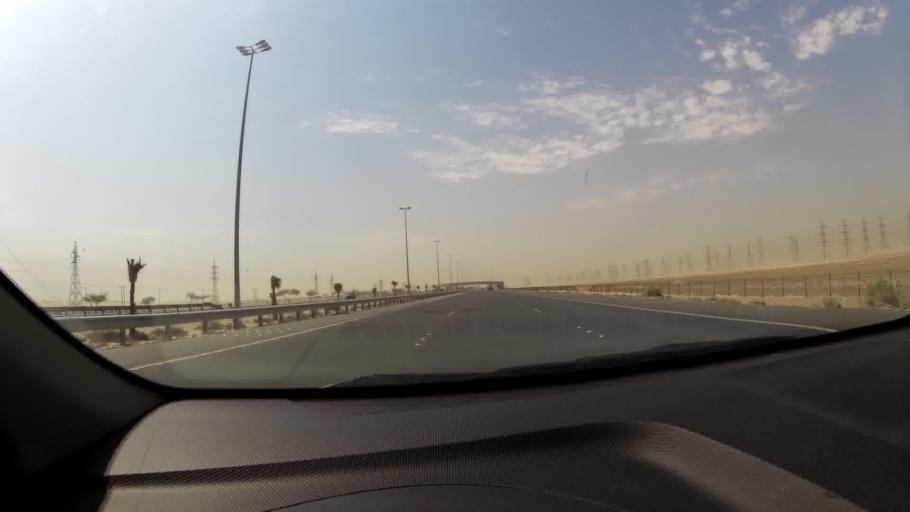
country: KW
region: Al Ahmadi
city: Al Fahahil
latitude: 28.7840
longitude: 48.2744
